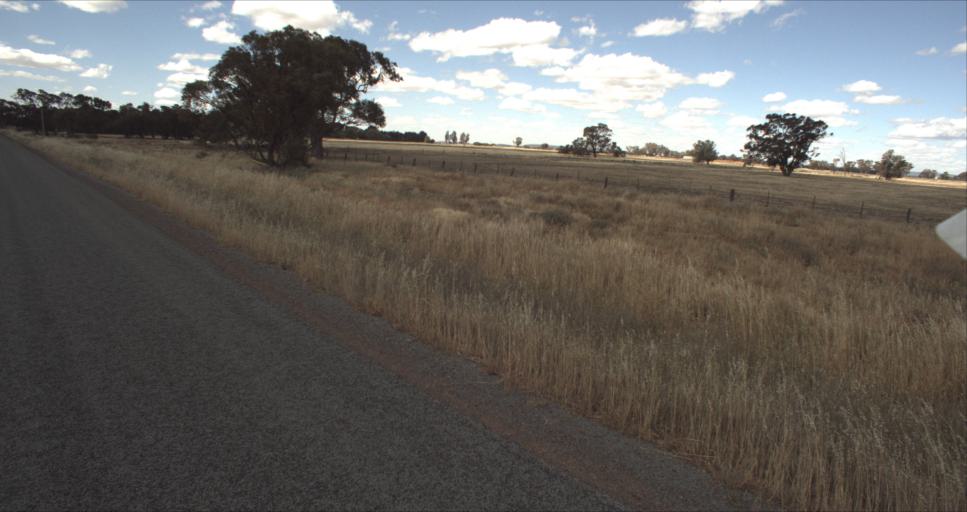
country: AU
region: New South Wales
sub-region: Leeton
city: Leeton
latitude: -34.4888
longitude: 146.2477
